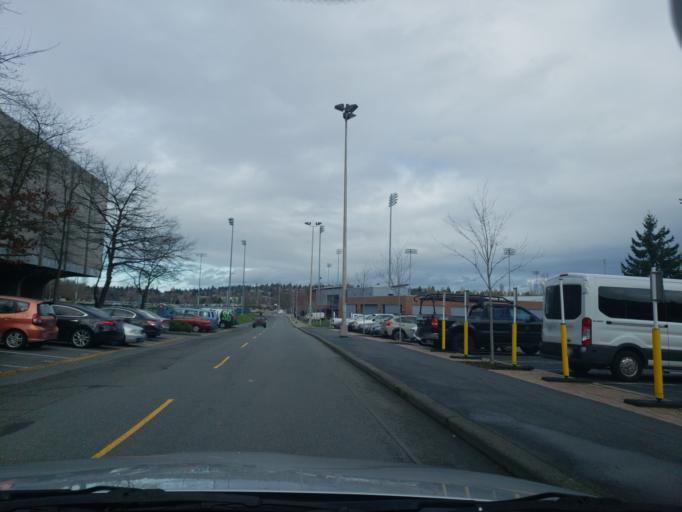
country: US
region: Washington
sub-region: King County
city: Seattle
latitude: 47.6533
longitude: -122.3002
